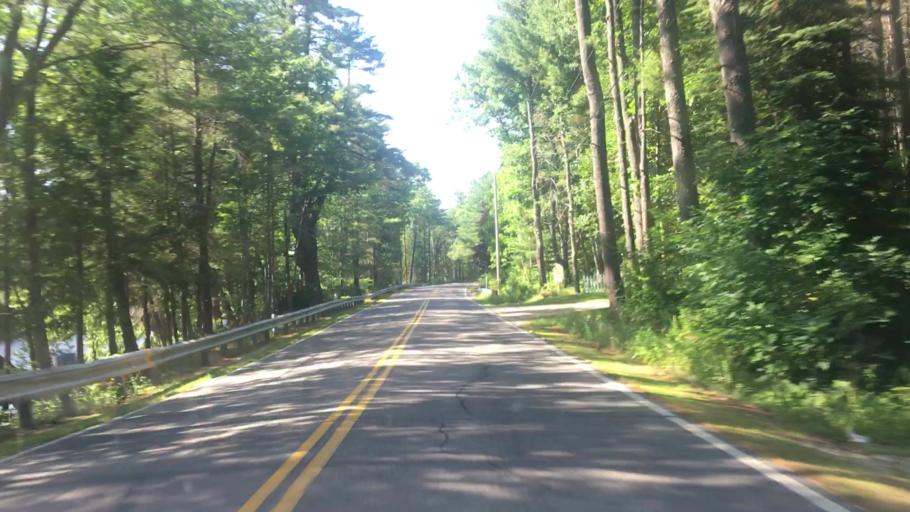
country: US
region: Maine
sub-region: York County
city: Hollis Center
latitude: 43.6580
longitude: -70.5967
